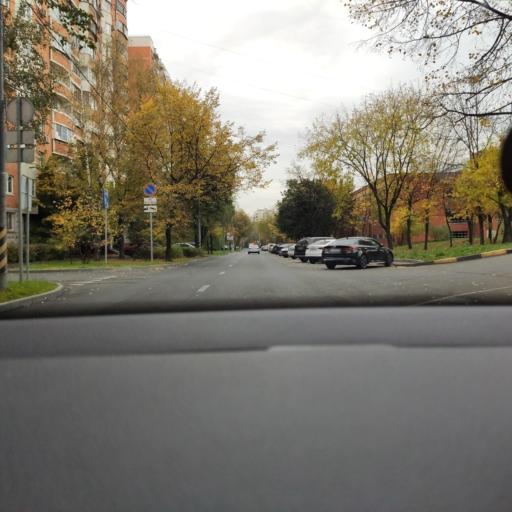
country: RU
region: Moscow
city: Kozeyevo
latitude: 55.8909
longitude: 37.6465
